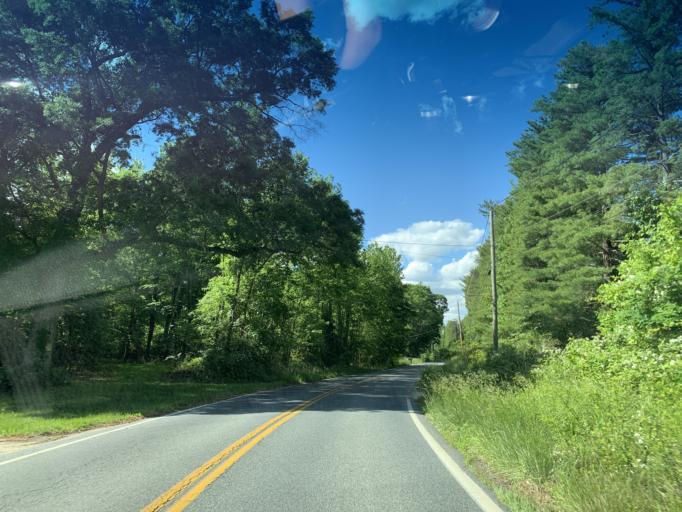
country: US
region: Maryland
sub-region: Cecil County
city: North East
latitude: 39.5663
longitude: -75.9390
